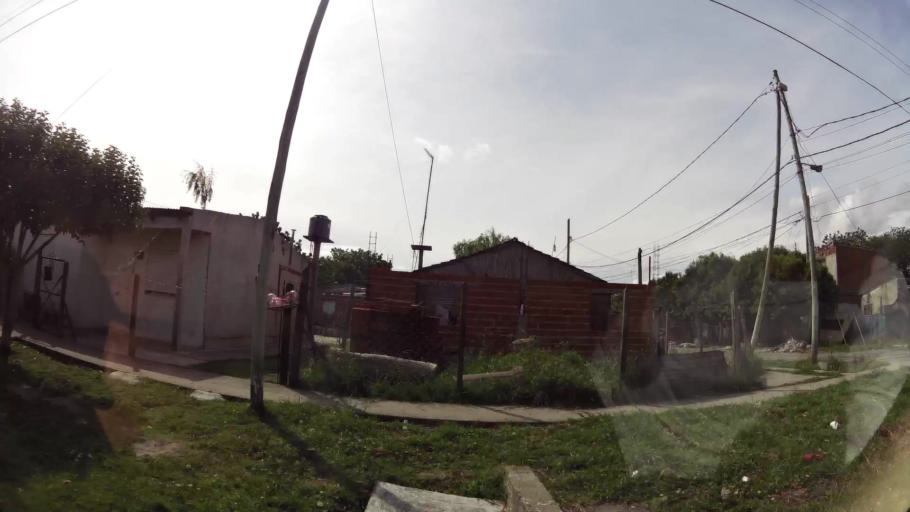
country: AR
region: Buenos Aires
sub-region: Partido de Quilmes
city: Quilmes
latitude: -34.7658
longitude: -58.2435
